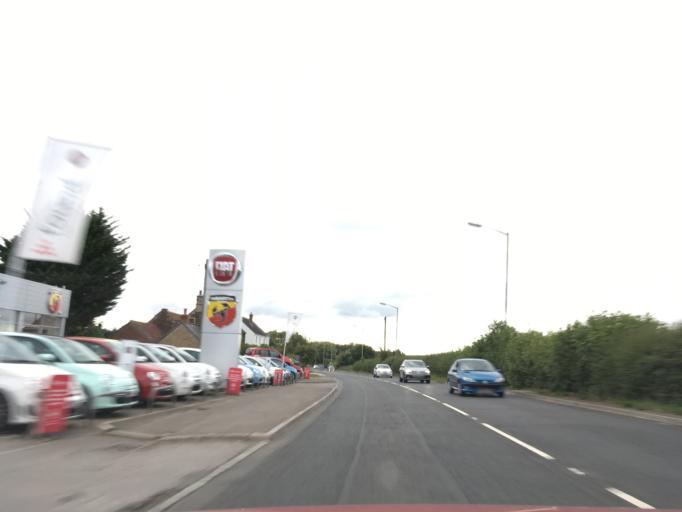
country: GB
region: England
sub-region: Wiltshire
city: Bremhill
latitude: 51.4405
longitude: -2.0754
